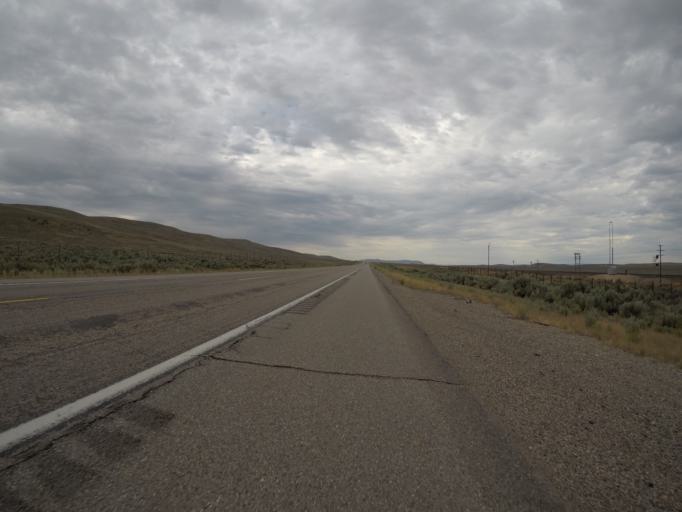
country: US
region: Utah
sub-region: Rich County
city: Randolph
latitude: 41.8405
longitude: -110.9765
